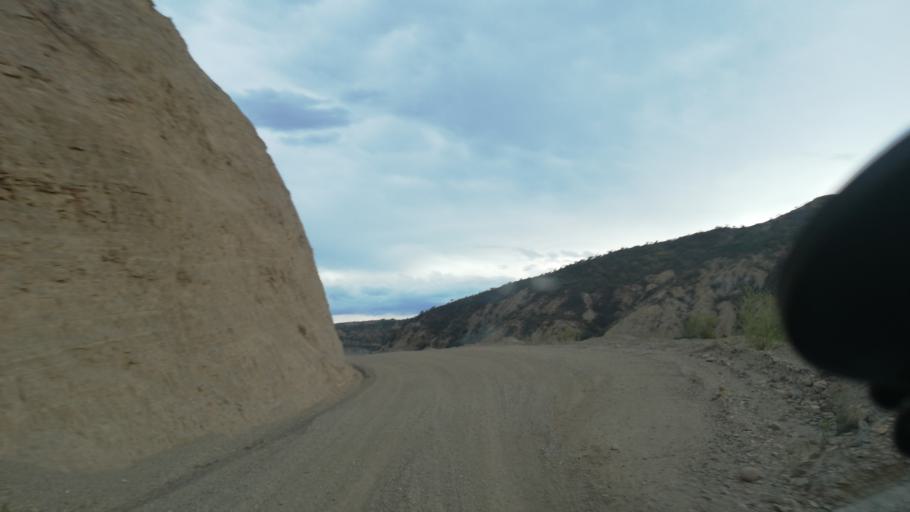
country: BO
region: Cochabamba
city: Sipe Sipe
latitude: -17.5648
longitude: -66.3736
